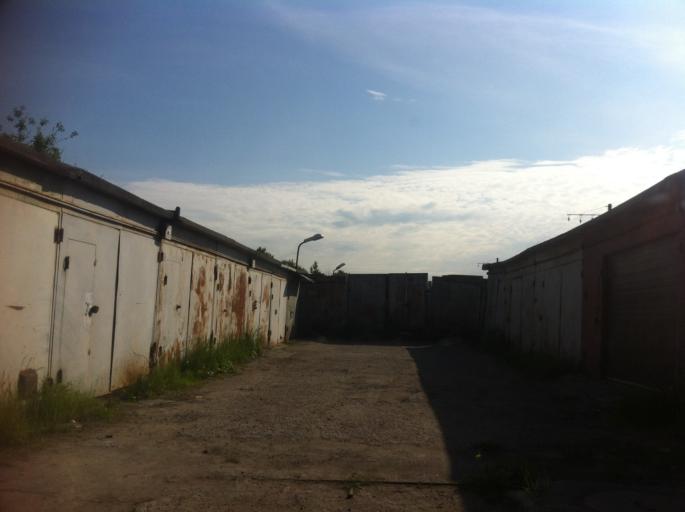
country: RU
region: St.-Petersburg
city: Dachnoye
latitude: 59.8329
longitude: 30.2585
